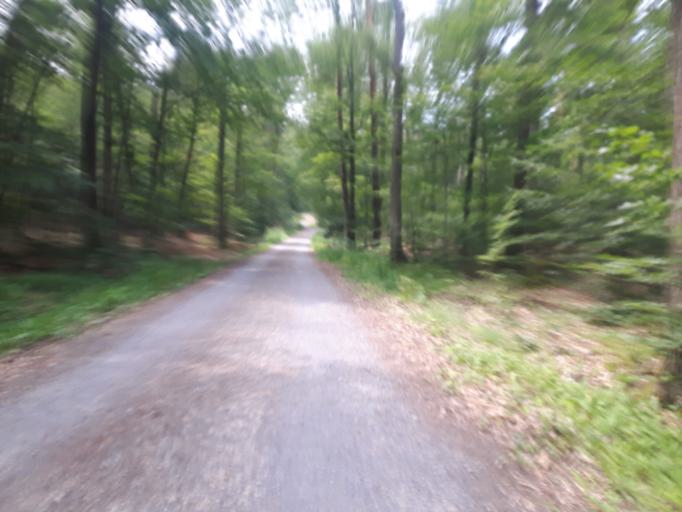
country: DE
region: Baden-Wuerttemberg
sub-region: Regierungsbezirk Stuttgart
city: Cleebronn
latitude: 49.0310
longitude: 9.0148
